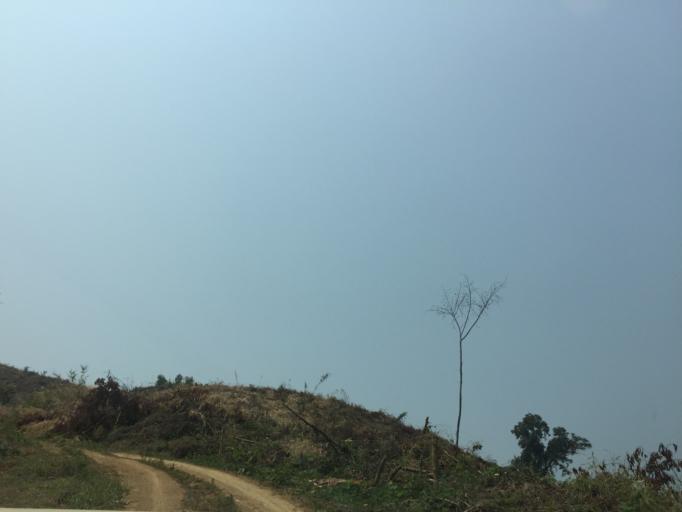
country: LA
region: Loungnamtha
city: Muang Nale
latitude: 20.6204
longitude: 101.6137
